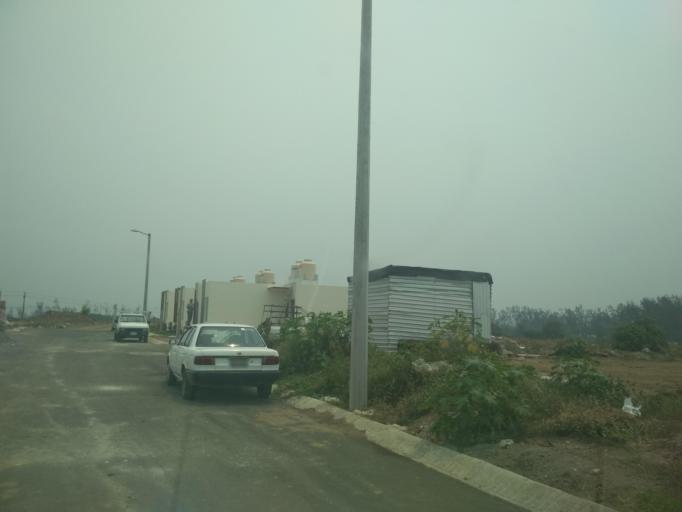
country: MX
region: Veracruz
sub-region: Veracruz
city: Las Amapolas
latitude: 19.1516
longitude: -96.2177
